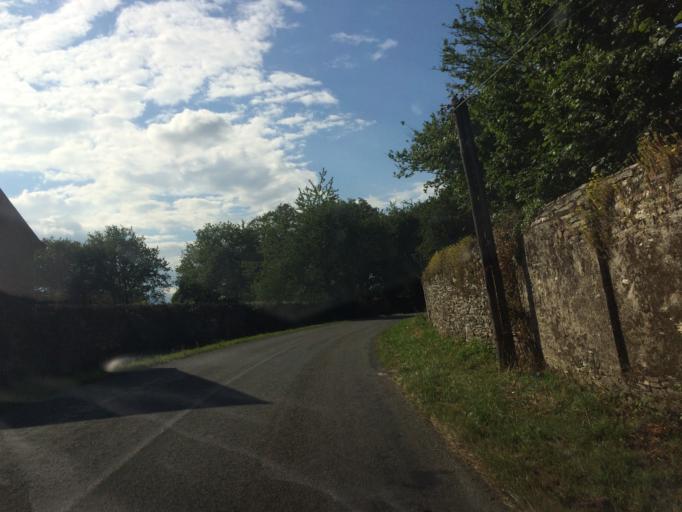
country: FR
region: Pays de la Loire
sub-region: Departement de la Loire-Atlantique
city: Plesse
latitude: 47.5522
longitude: -1.8934
